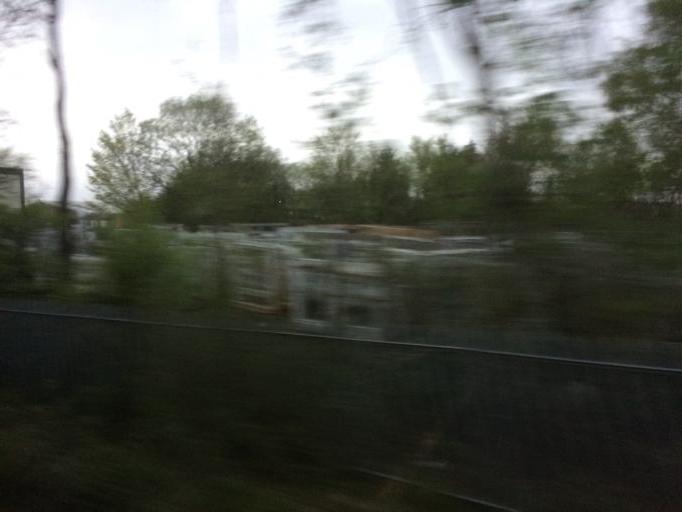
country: GB
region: Scotland
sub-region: North Lanarkshire
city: Cumbernauld
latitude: 55.9814
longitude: -3.9475
